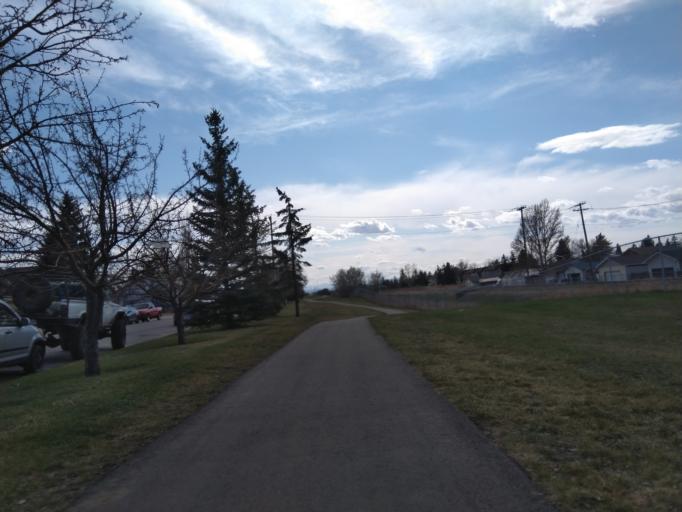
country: CA
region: Alberta
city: Chestermere
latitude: 51.0501
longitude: -113.9302
